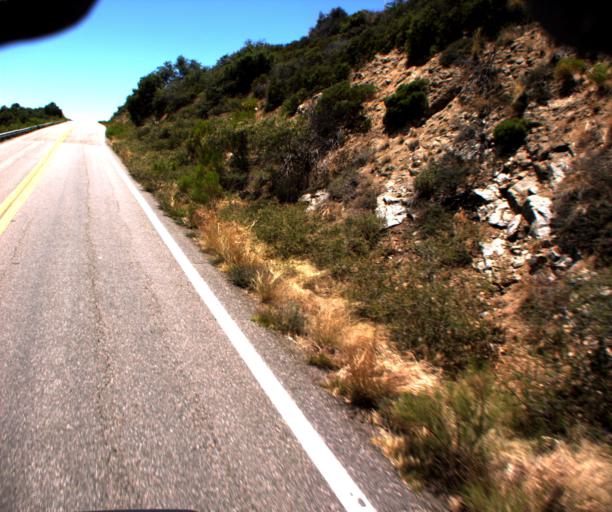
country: US
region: Arizona
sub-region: Gila County
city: Globe
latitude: 33.2730
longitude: -110.7620
